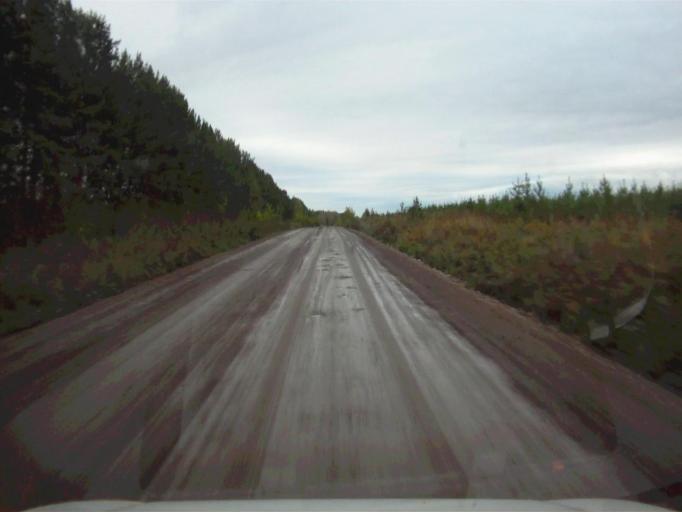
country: RU
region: Sverdlovsk
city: Mikhaylovsk
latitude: 56.1453
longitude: 59.2824
